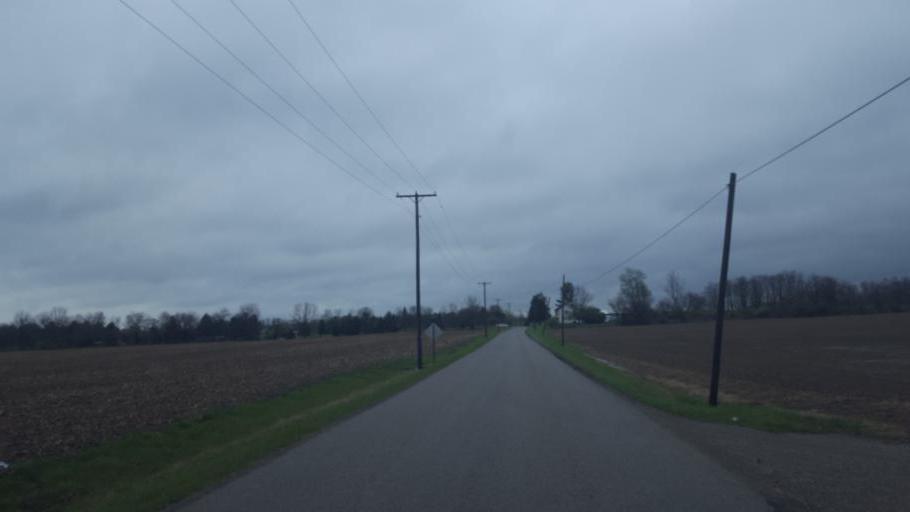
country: US
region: Ohio
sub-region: Morrow County
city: Cardington
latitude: 40.5173
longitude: -82.8618
